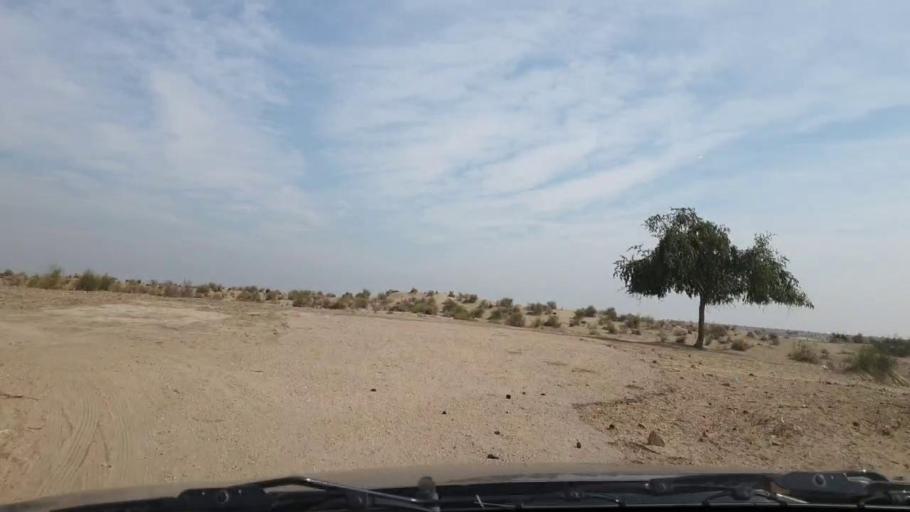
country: PK
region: Sindh
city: Jam Sahib
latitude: 26.2922
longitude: 68.6977
